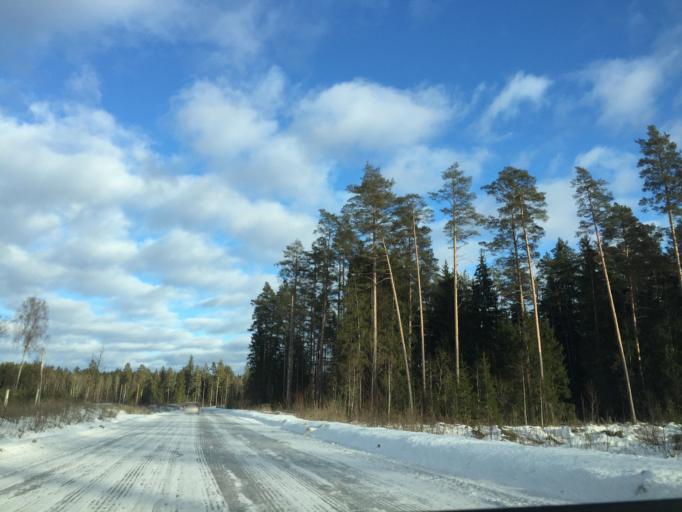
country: LV
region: Ogre
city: Jumprava
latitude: 56.5909
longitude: 24.9780
